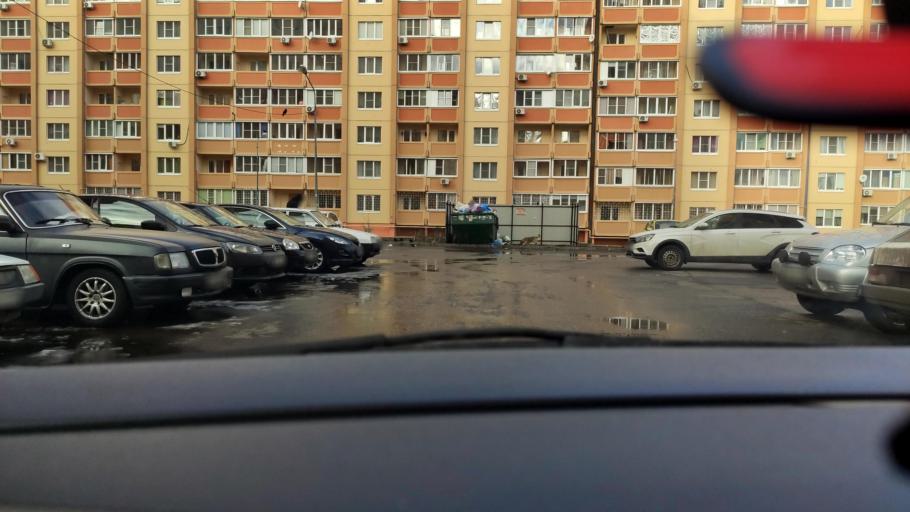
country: RU
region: Voronezj
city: Pridonskoy
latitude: 51.6220
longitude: 39.0645
